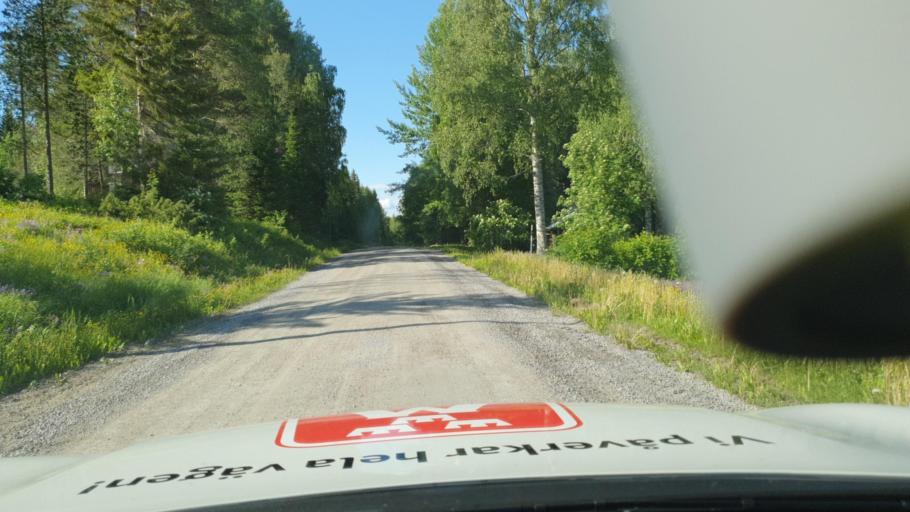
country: SE
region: Vaesterbotten
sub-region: Vannas Kommun
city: Vaennaes
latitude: 63.8164
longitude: 19.6289
